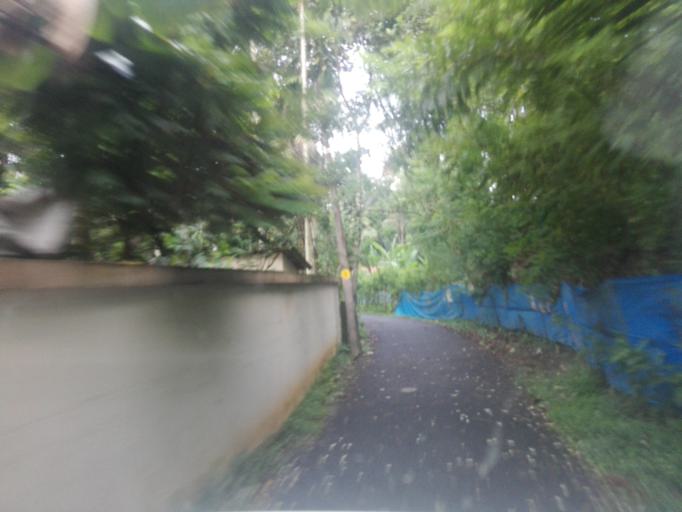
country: IN
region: Kerala
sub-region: Alappuzha
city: Arukutti
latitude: 9.8289
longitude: 76.3911
